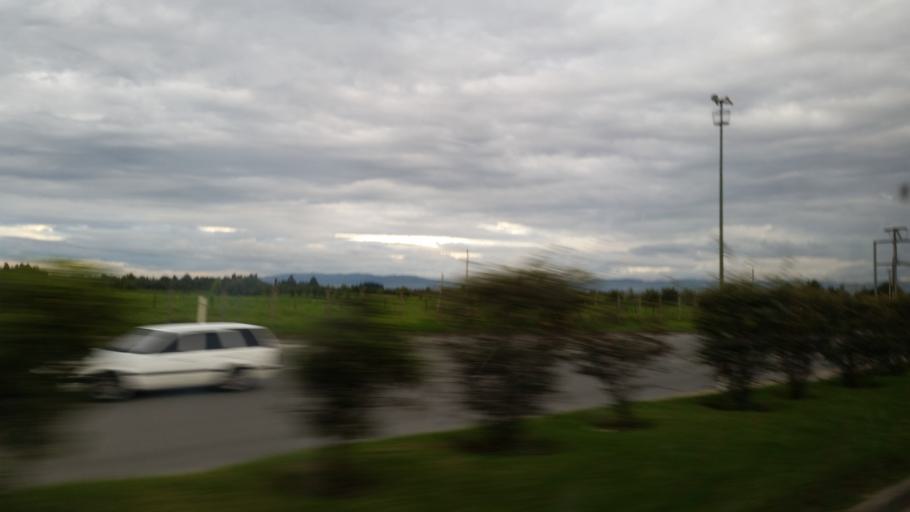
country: CO
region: Cundinamarca
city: Funza
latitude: 4.6975
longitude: -74.1773
